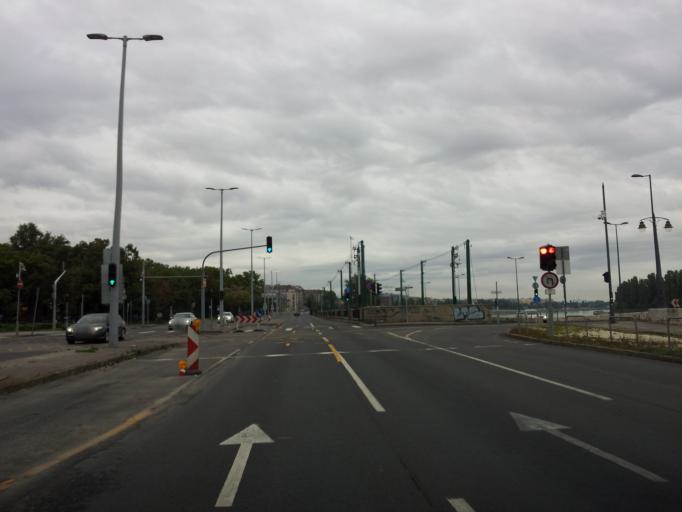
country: HU
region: Budapest
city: Budapest II. keruelet
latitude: 47.5163
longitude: 19.0384
